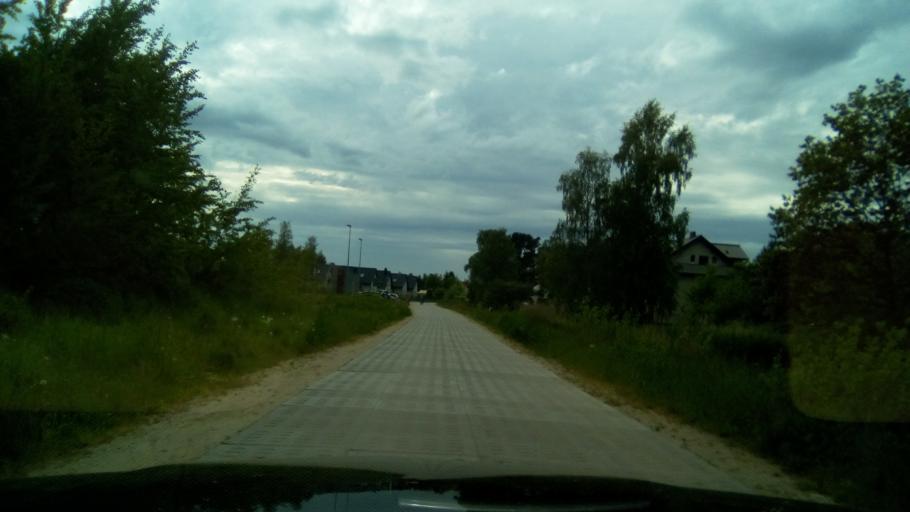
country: PL
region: Pomeranian Voivodeship
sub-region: Powiat pucki
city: Krokowa
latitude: 54.8267
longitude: 18.0929
